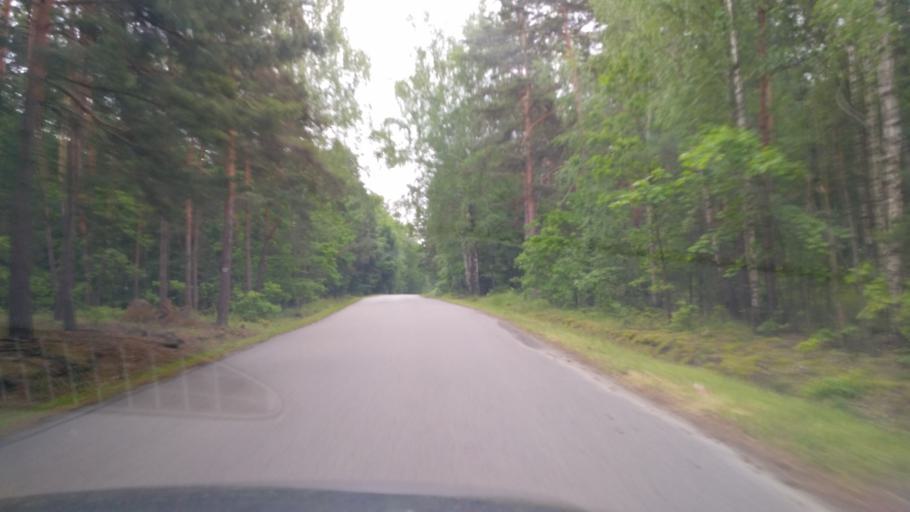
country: PL
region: Subcarpathian Voivodeship
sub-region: Powiat kolbuszowski
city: Niwiska
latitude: 50.2154
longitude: 21.6450
